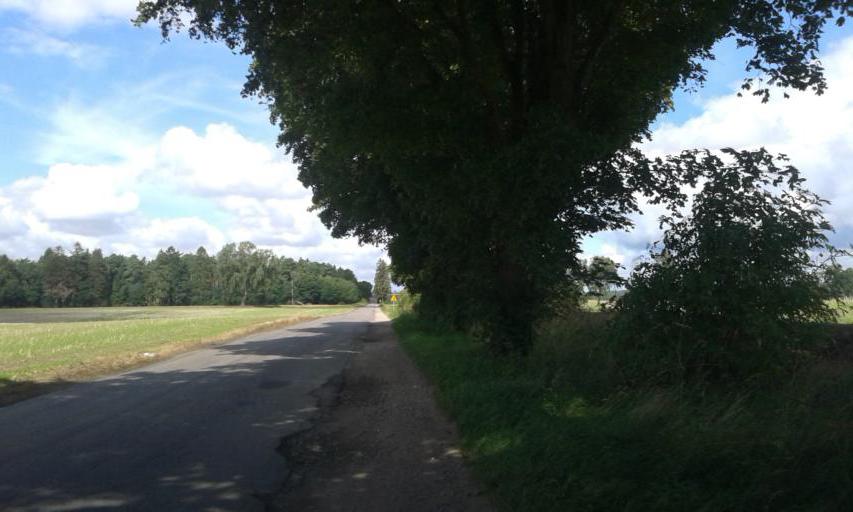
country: PL
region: West Pomeranian Voivodeship
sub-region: Powiat slawienski
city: Slawno
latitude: 54.2927
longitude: 16.6495
